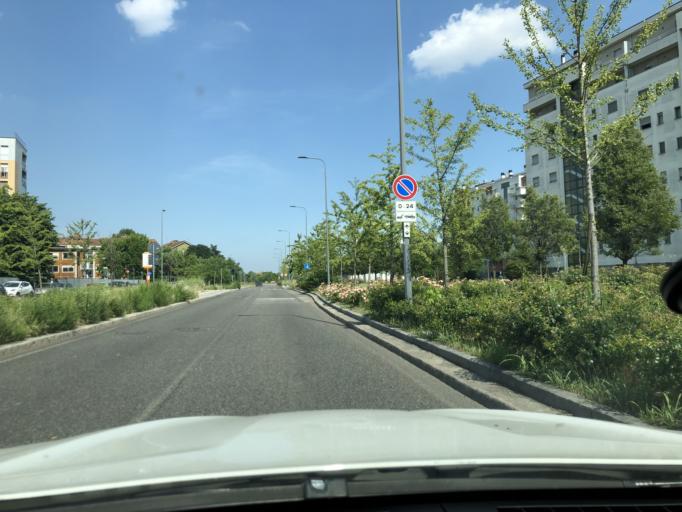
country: IT
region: Lombardy
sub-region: Citta metropolitana di Milano
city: Novate Milanese
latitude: 45.5114
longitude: 9.1435
